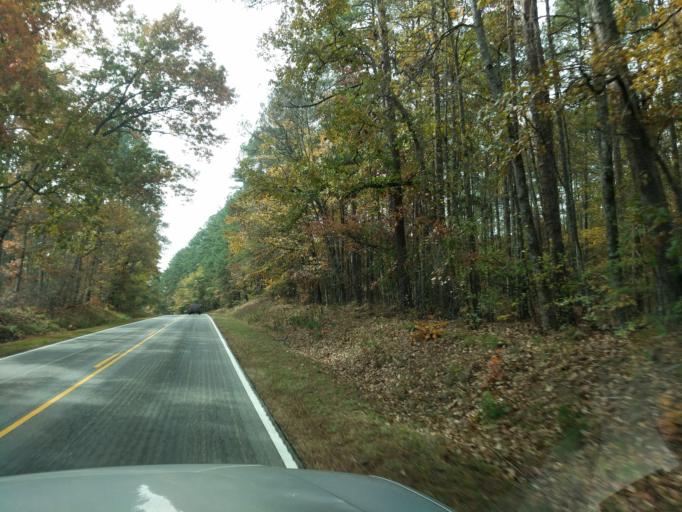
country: US
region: South Carolina
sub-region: Laurens County
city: Joanna
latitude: 34.2524
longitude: -81.8654
